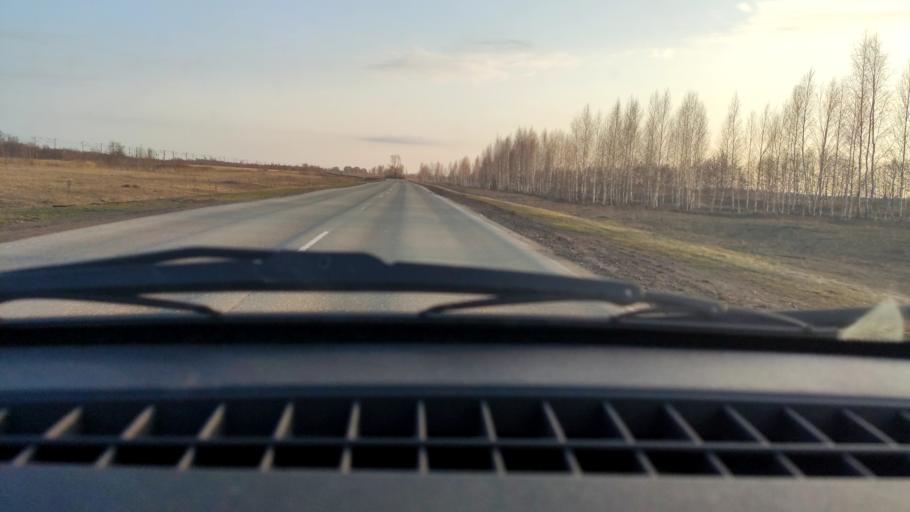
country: RU
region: Bashkortostan
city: Chishmy
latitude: 54.4377
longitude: 55.2378
